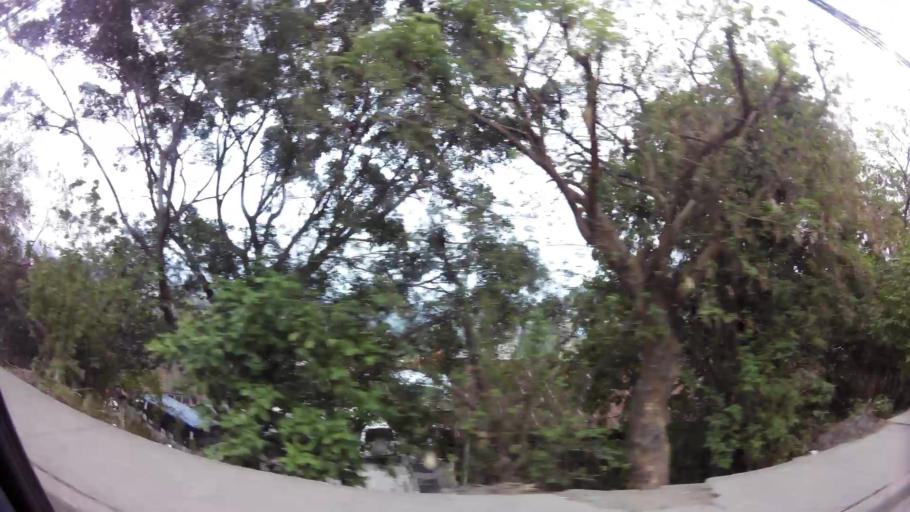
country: HN
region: Francisco Morazan
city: Tegucigalpa
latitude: 14.0829
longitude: -87.2258
